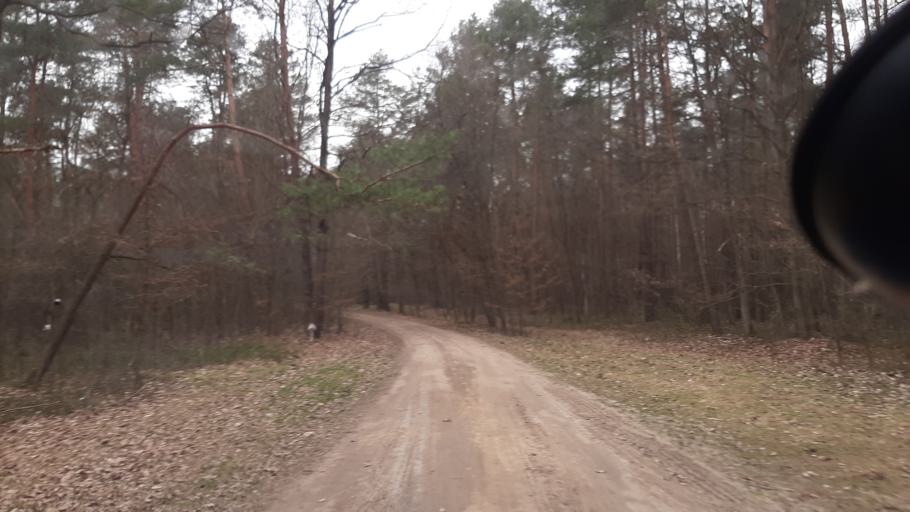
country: PL
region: Lublin Voivodeship
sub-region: Powiat lubartowski
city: Abramow
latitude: 51.4436
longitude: 22.3440
